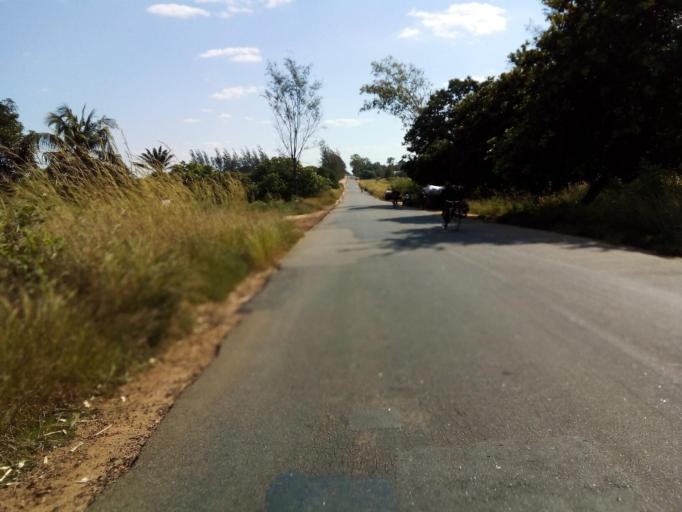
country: MZ
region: Zambezia
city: Quelimane
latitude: -17.5765
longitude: 36.6483
